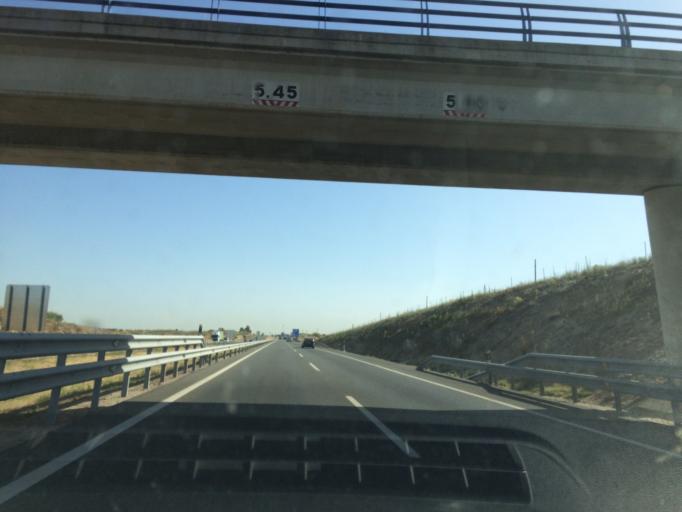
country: ES
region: Castille-La Mancha
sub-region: Province of Toledo
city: Valmojado
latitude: 40.2282
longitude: -4.0710
